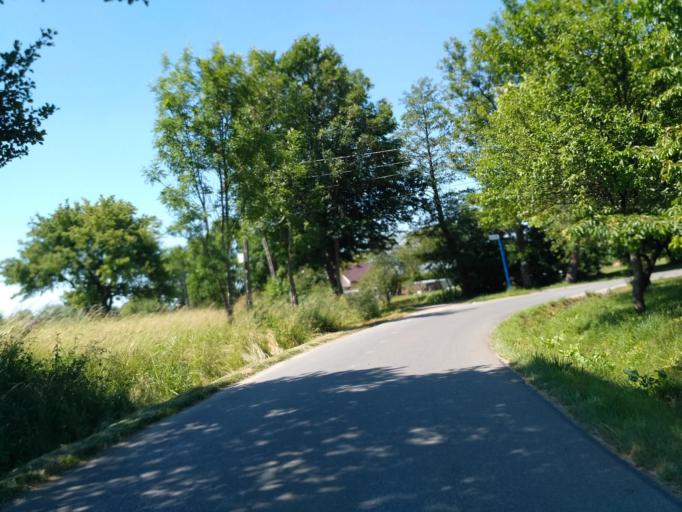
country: PL
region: Subcarpathian Voivodeship
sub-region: Powiat krosnienski
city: Odrzykon
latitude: 49.7245
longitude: 21.7709
